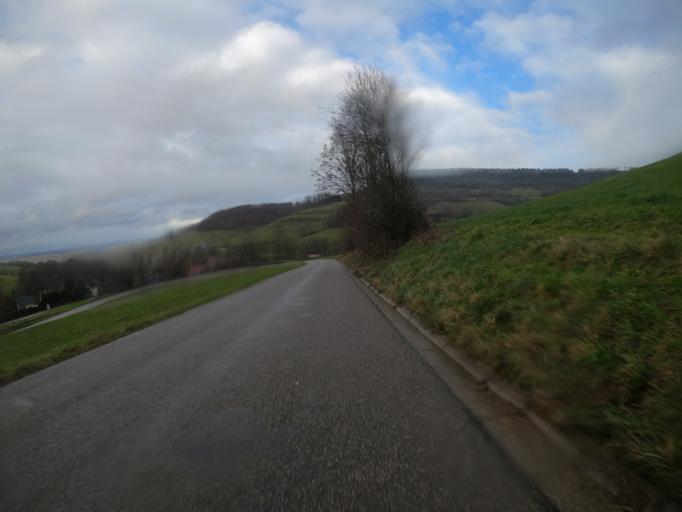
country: DE
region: Baden-Wuerttemberg
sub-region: Regierungsbezirk Stuttgart
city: Waldstetten
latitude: 48.7426
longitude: 9.8414
